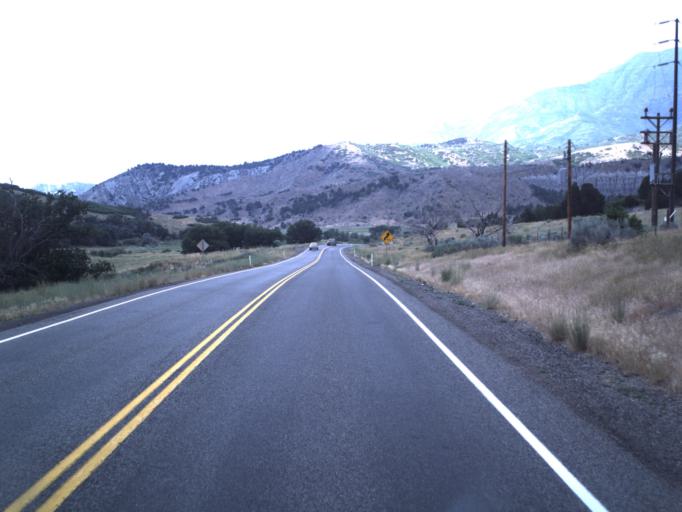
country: US
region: Utah
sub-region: Juab County
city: Nephi
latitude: 39.7136
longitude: -111.7214
